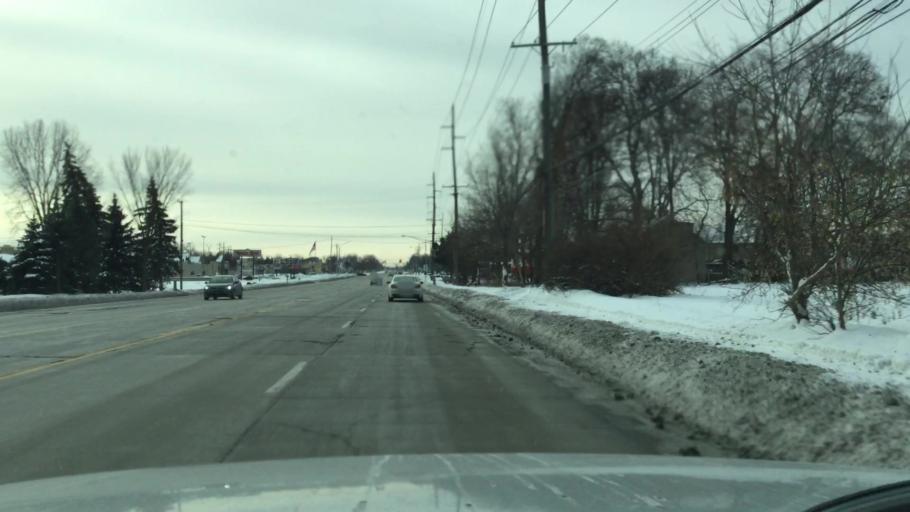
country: US
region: Michigan
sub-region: Oakland County
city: Troy
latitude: 42.5957
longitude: -83.1294
